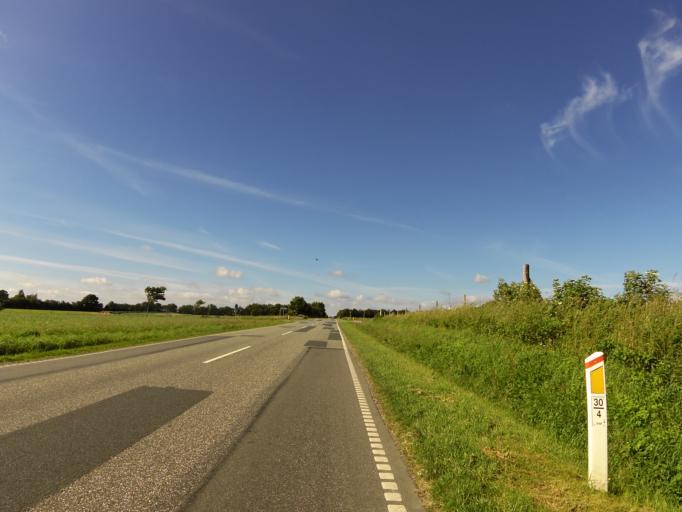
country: DK
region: South Denmark
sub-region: Tonder Kommune
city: Toftlund
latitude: 55.0964
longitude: 9.1751
